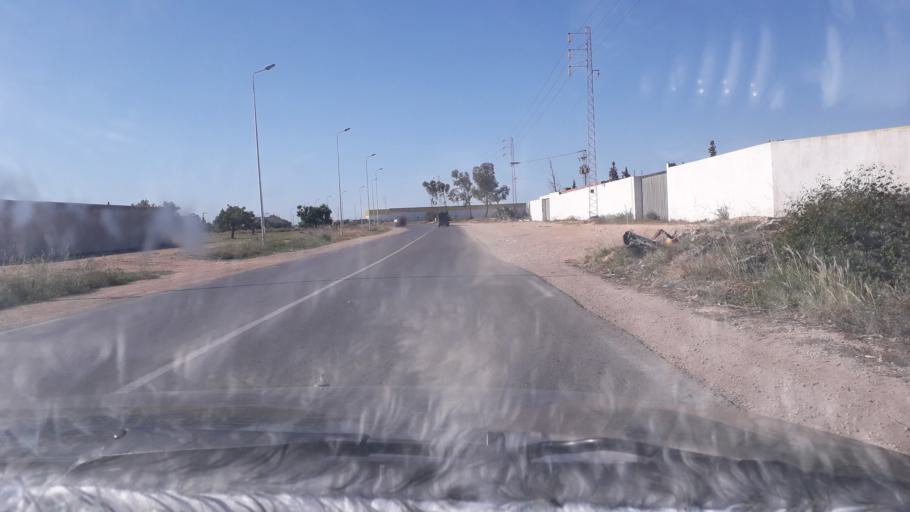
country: TN
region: Safaqis
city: Al Qarmadah
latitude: 34.8732
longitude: 10.7559
